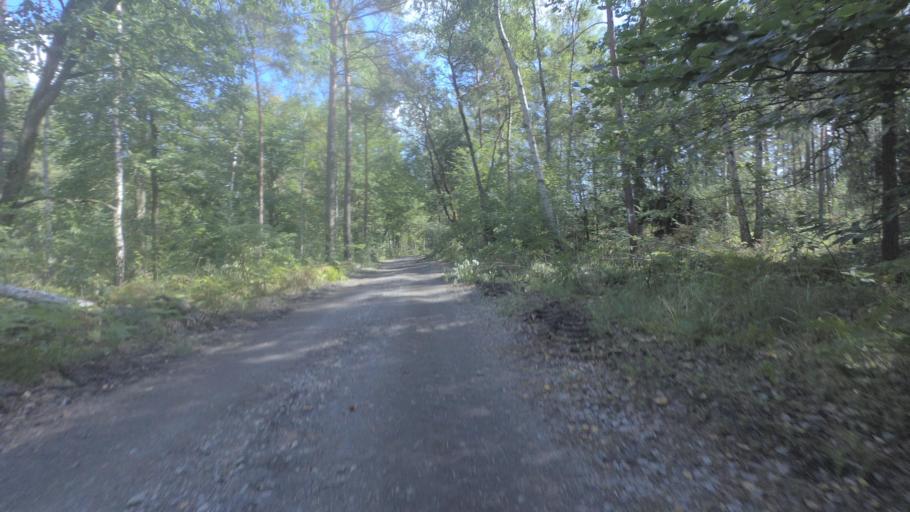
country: DE
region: Brandenburg
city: Halbe
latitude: 52.1522
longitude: 13.7327
